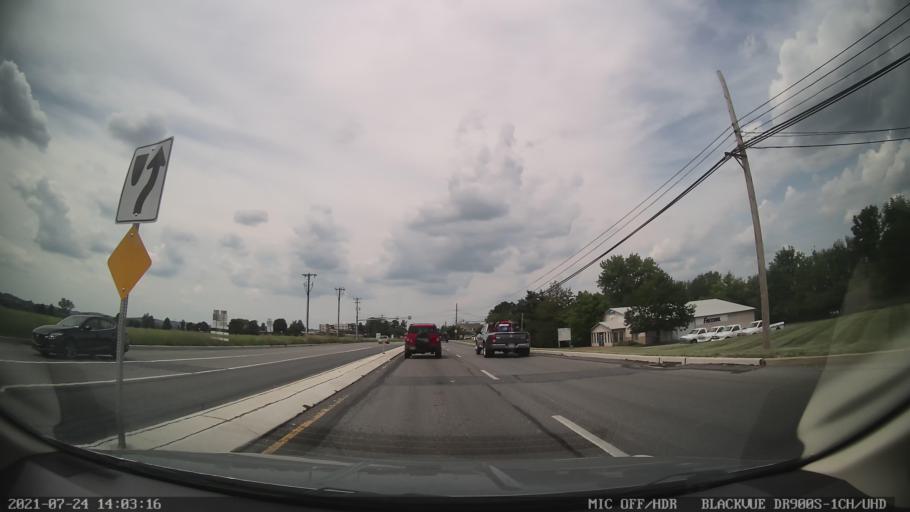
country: US
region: Pennsylvania
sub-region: Lehigh County
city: Trexlertown
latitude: 40.5654
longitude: -75.6132
